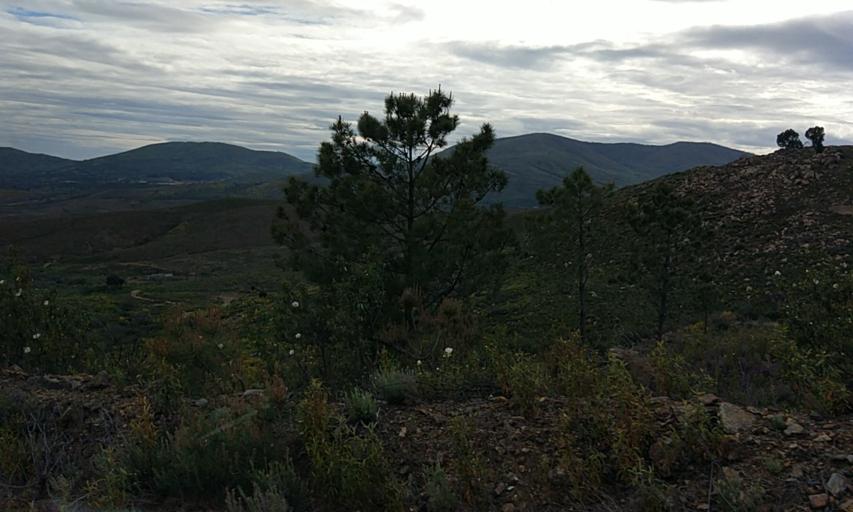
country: ES
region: Extremadura
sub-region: Provincia de Caceres
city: Acebo
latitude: 40.2152
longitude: -6.6759
